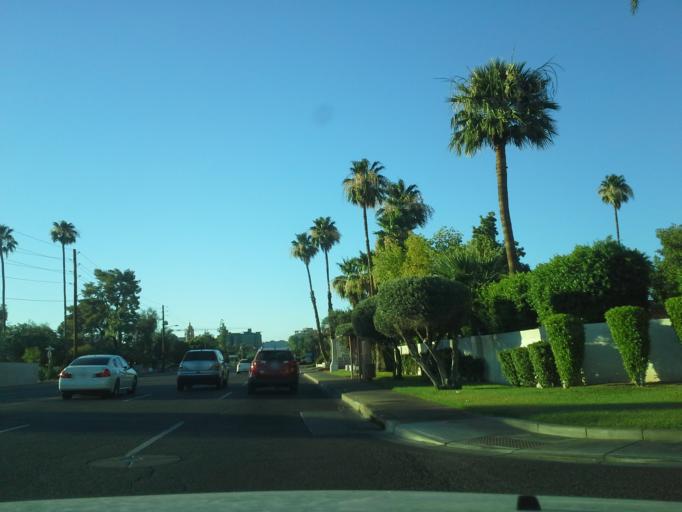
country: US
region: Arizona
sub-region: Maricopa County
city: Phoenix
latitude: 33.4985
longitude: -112.0302
